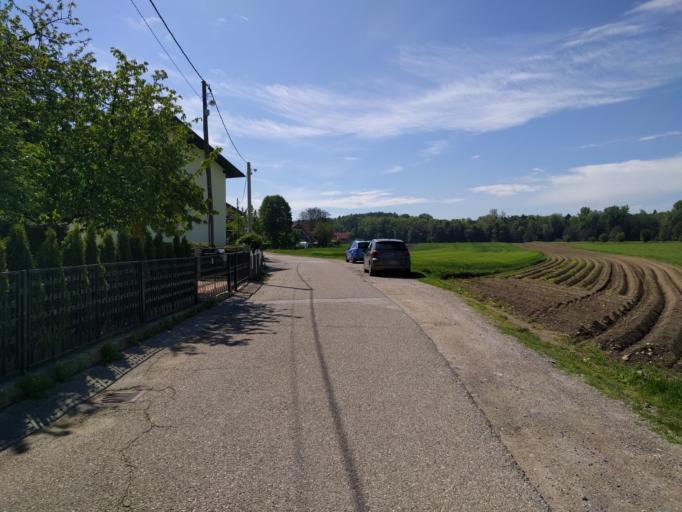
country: SI
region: Miklavz na Dravskem Polju
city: Miklavz na Dravskem Polju
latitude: 46.5341
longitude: 15.6894
